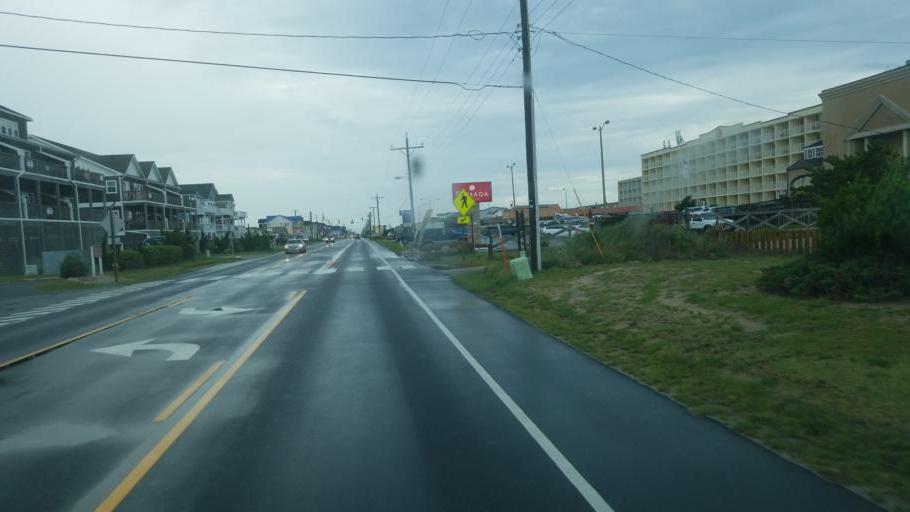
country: US
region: North Carolina
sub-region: Dare County
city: Kill Devil Hills
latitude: 35.9982
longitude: -75.6478
